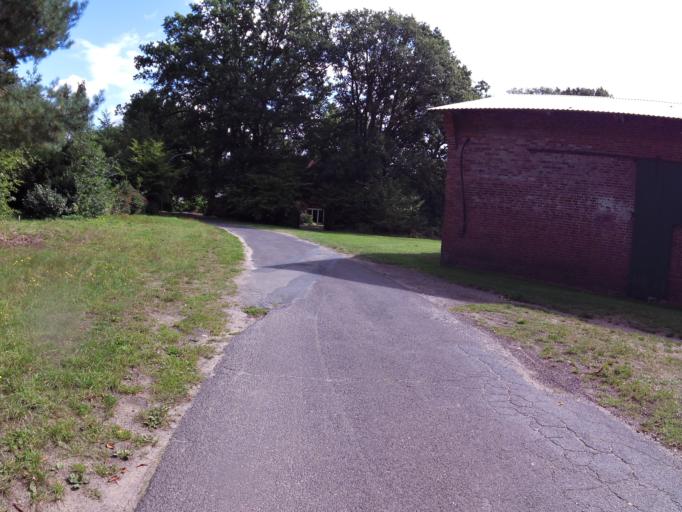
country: DE
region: Lower Saxony
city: Heeslingen
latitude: 53.3165
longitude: 9.3030
